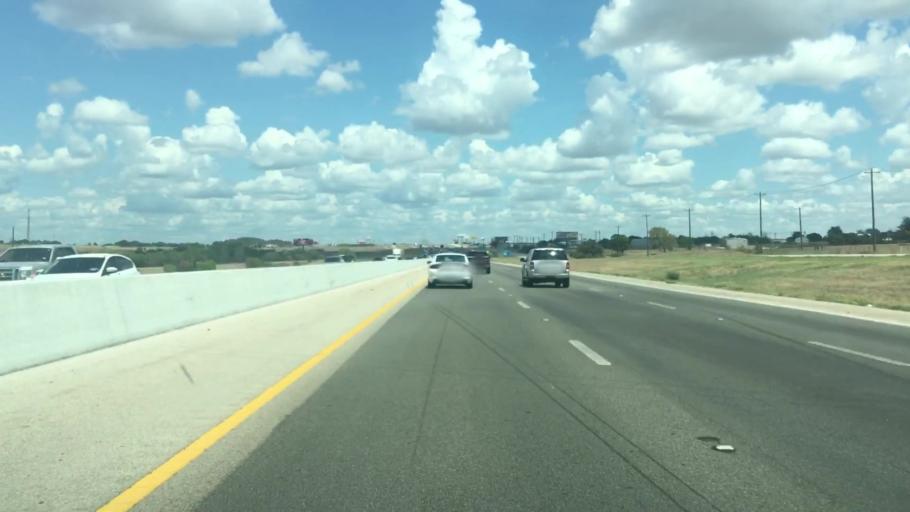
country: US
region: Texas
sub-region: Williamson County
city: Serenada
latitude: 30.7593
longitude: -97.6311
